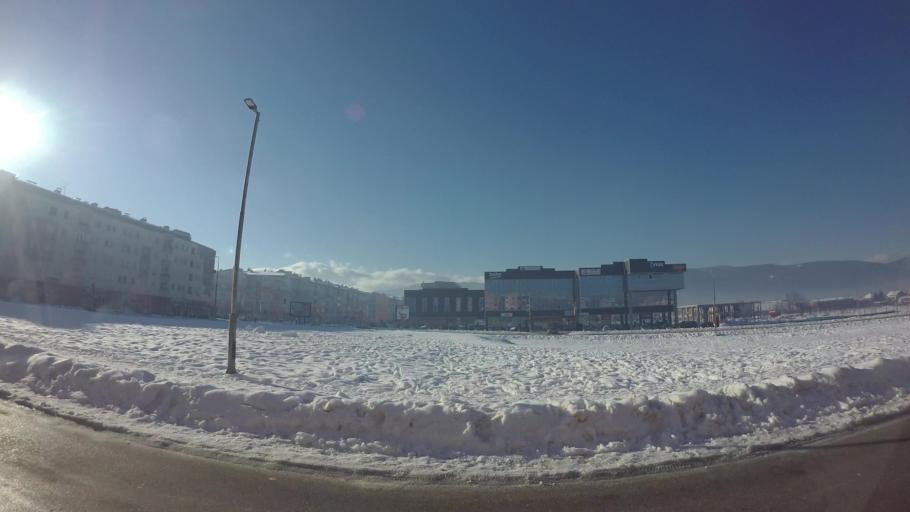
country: BA
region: Federation of Bosnia and Herzegovina
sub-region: Kanton Sarajevo
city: Sarajevo
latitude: 43.8200
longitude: 18.3617
